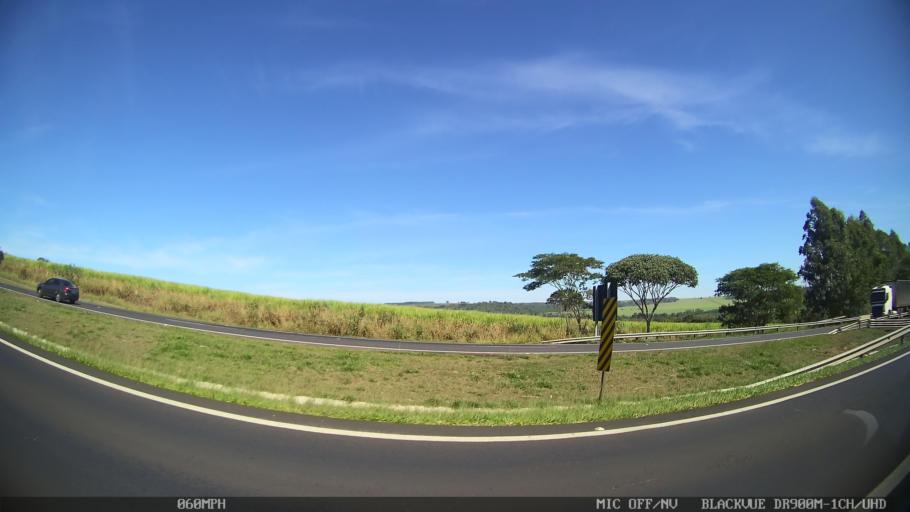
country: BR
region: Sao Paulo
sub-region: Santa Rita Do Passa Quatro
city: Santa Rita do Passa Quatro
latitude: -21.7537
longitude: -47.5666
